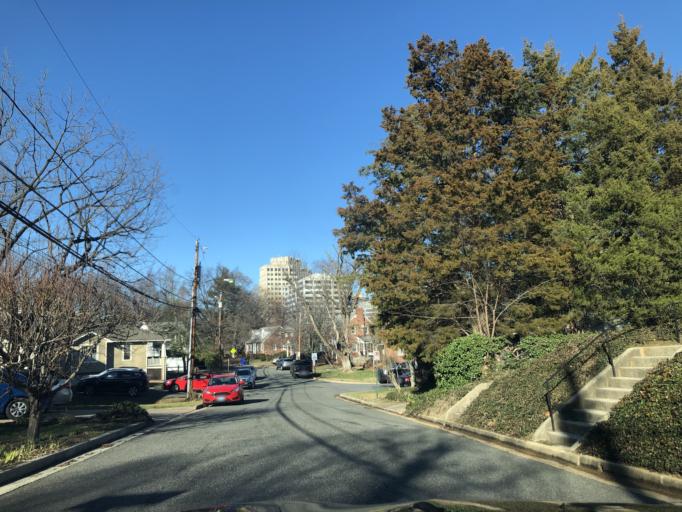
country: US
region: Virginia
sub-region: Arlington County
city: Arlington
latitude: 38.8794
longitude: -77.1192
